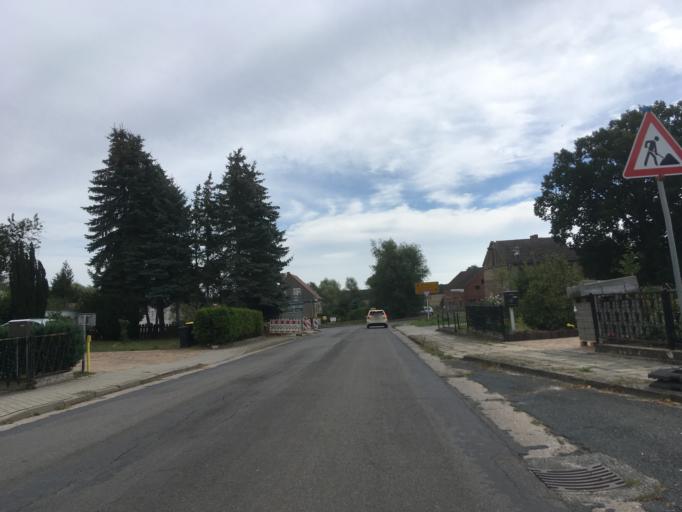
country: DE
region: Brandenburg
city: Mittenwalde
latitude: 53.2163
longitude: 13.6926
